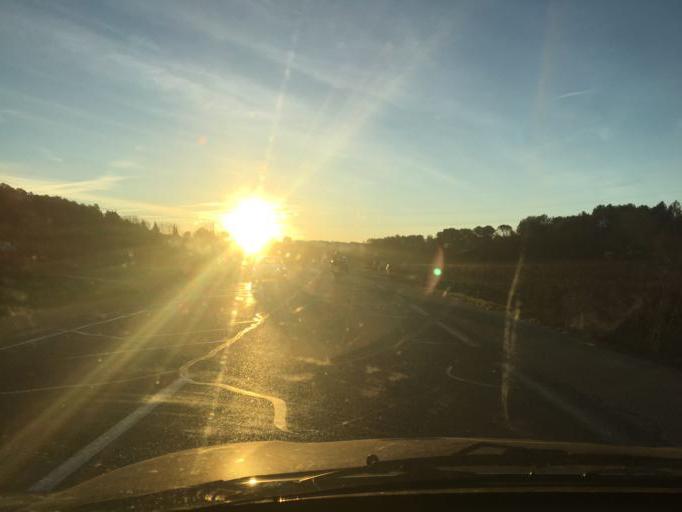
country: FR
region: Provence-Alpes-Cote d'Azur
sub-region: Departement du Var
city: Lorgues
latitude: 43.4699
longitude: 6.3826
